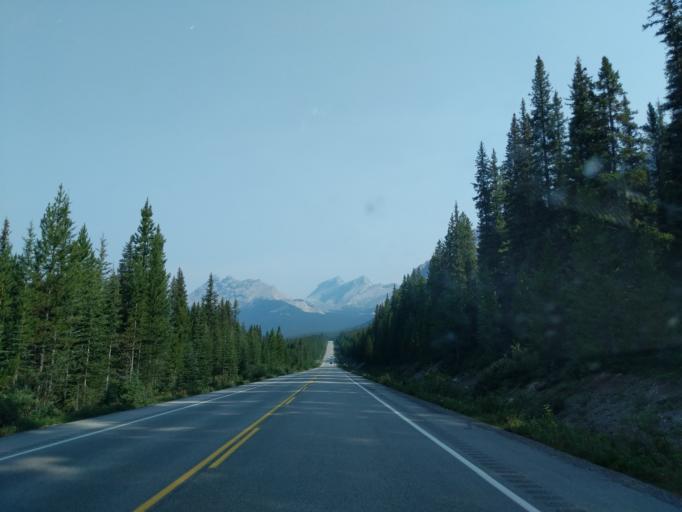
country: CA
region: Alberta
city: Lake Louise
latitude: 51.5983
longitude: -116.3078
